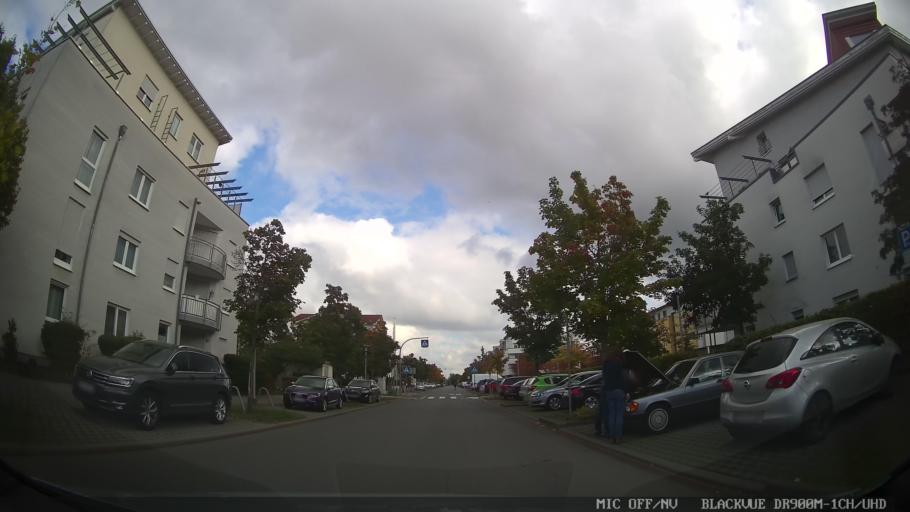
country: DE
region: Hesse
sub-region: Regierungsbezirk Darmstadt
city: Ginsheim-Gustavsburg
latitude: 49.9744
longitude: 8.3364
